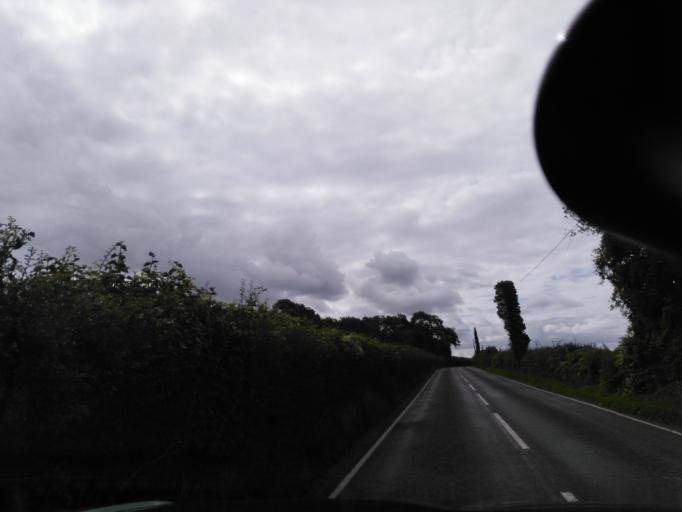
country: GB
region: England
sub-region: Dorset
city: Blandford Forum
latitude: 50.8971
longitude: -2.1557
